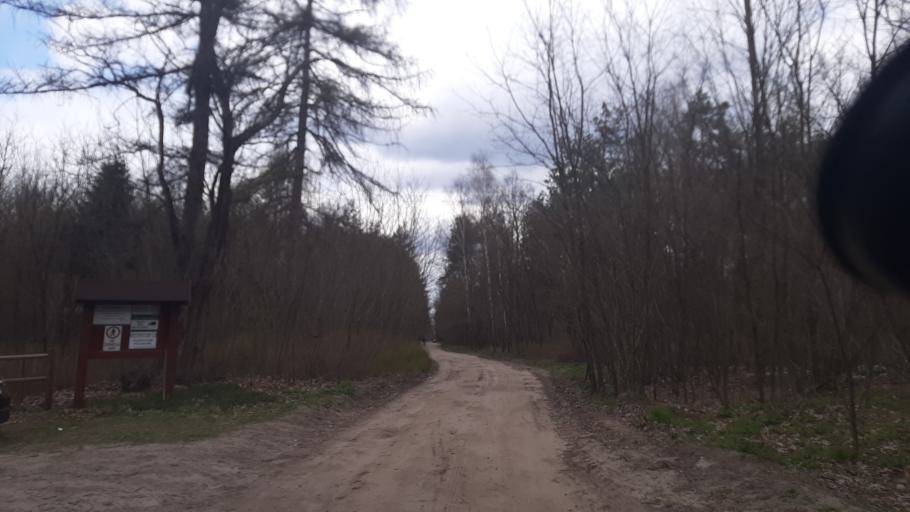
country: PL
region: Lublin Voivodeship
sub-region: Powiat lubelski
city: Niemce
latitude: 51.3890
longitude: 22.5650
